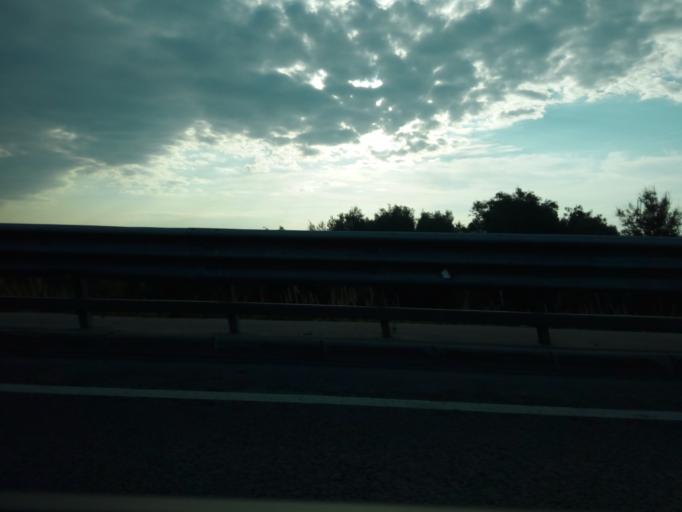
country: RU
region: Moscow
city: Khimki
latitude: 55.9528
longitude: 37.4146
